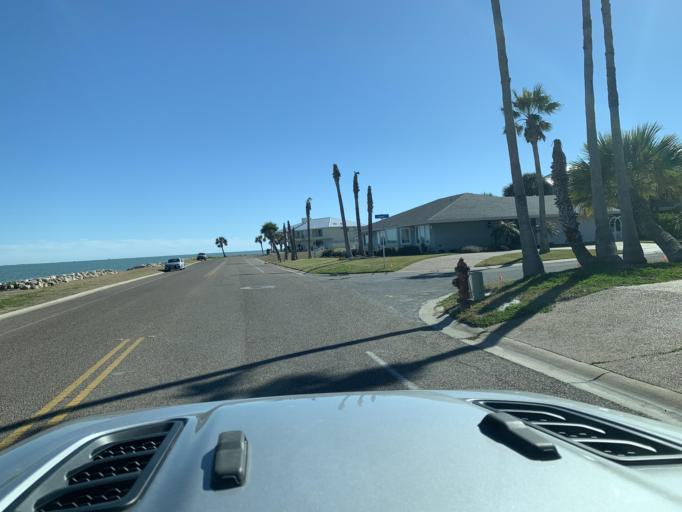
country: US
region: Texas
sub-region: Aransas County
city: Fulton
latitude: 28.0342
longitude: -97.0255
